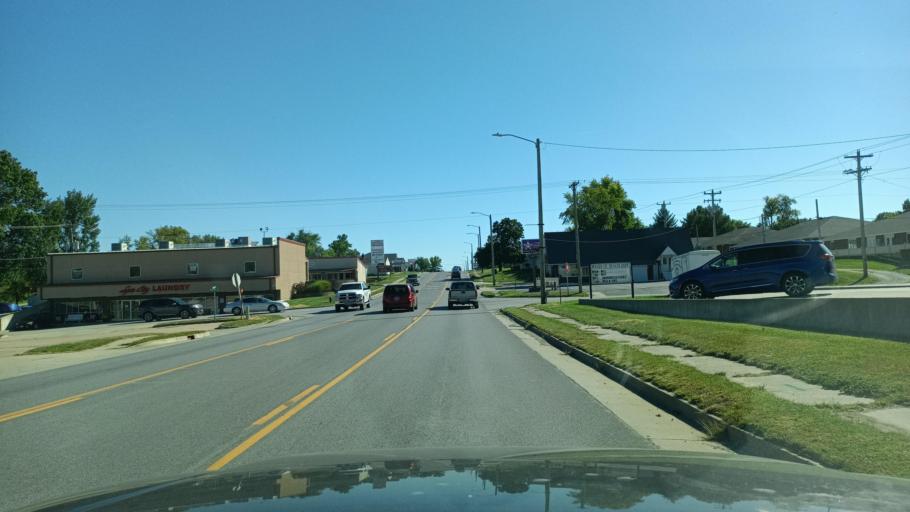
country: US
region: Missouri
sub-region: Macon County
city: Macon
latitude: 39.7429
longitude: -92.4652
